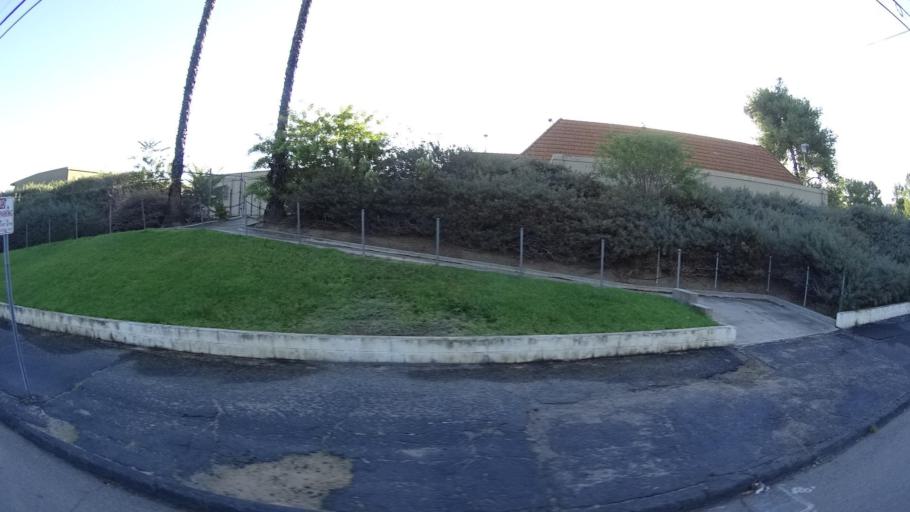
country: US
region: California
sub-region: San Diego County
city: Lakeside
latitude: 32.8539
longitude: -116.9116
